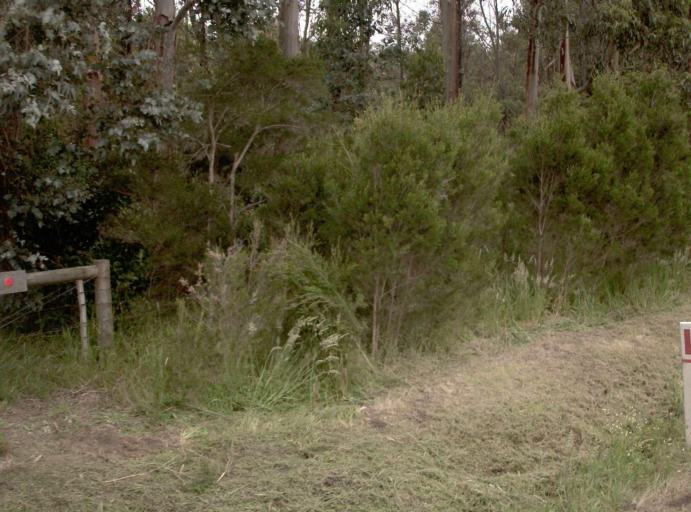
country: AU
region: Victoria
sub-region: Bass Coast
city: North Wonthaggi
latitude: -38.5516
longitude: 145.6551
